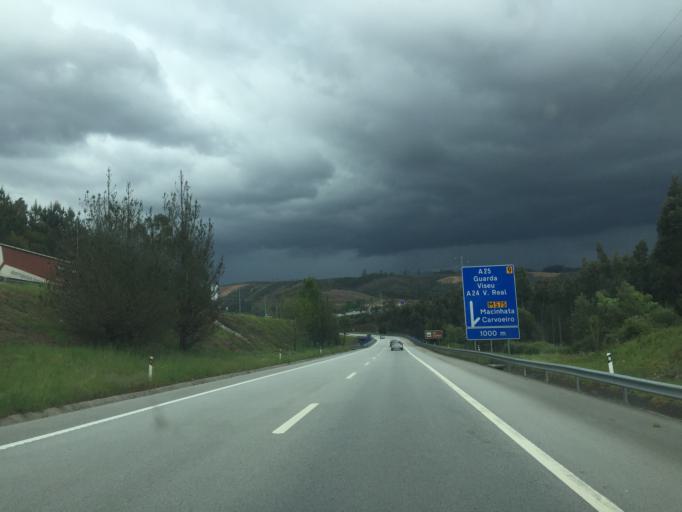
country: PT
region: Aveiro
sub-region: Albergaria-A-Velha
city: Albergaria-a-Velha
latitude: 40.6771
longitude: -8.4484
